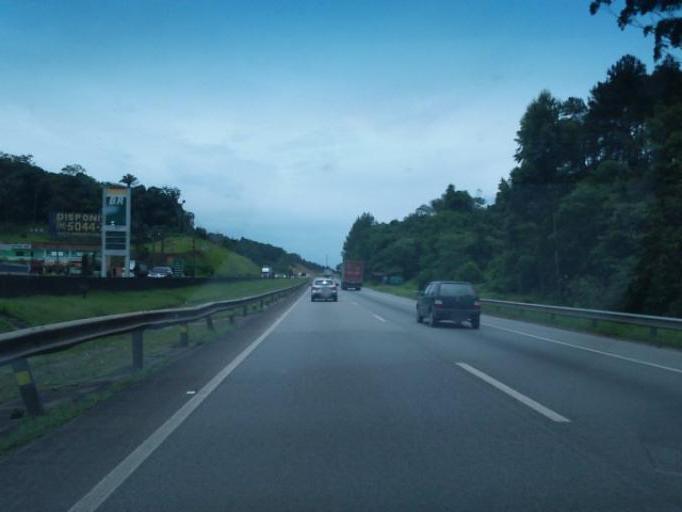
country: BR
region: Sao Paulo
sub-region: Juquitiba
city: Juquitiba
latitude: -23.9343
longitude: -47.0164
